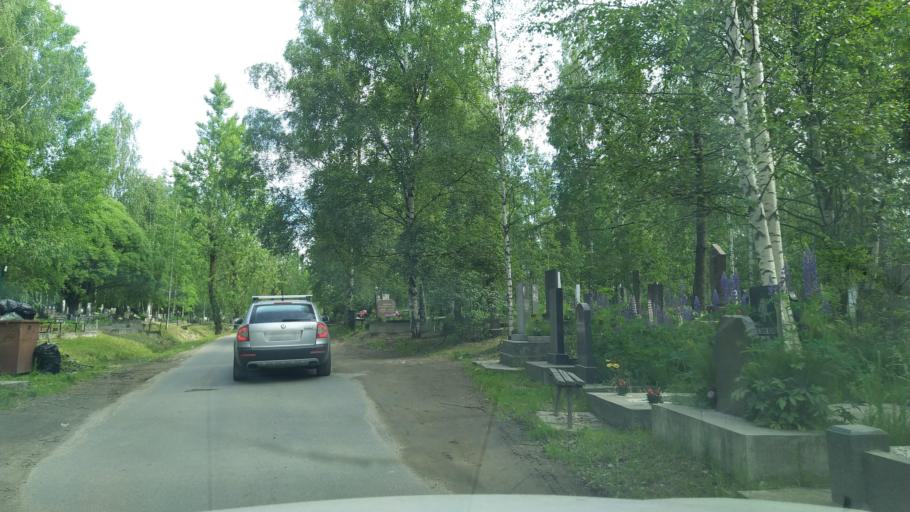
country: RU
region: St.-Petersburg
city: Dachnoye
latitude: 59.7652
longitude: 30.2617
